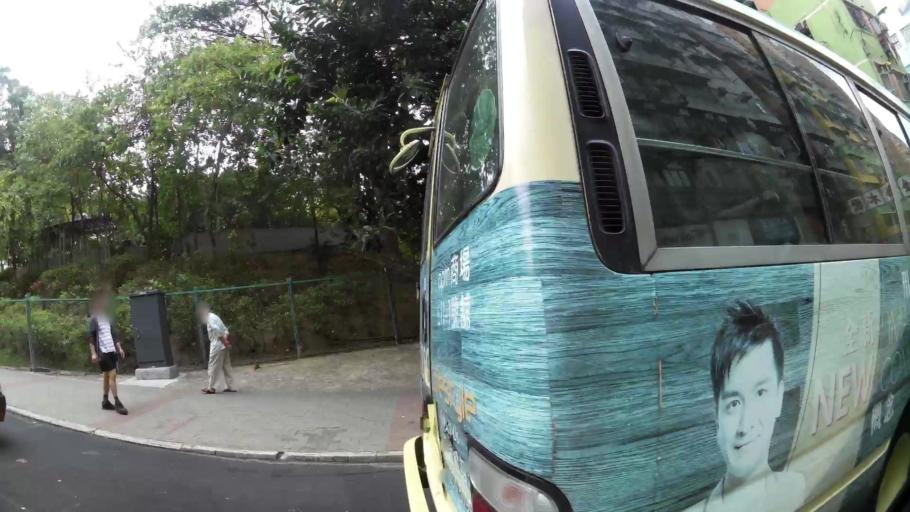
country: HK
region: Kowloon City
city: Kowloon
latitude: 22.3162
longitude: 114.2235
